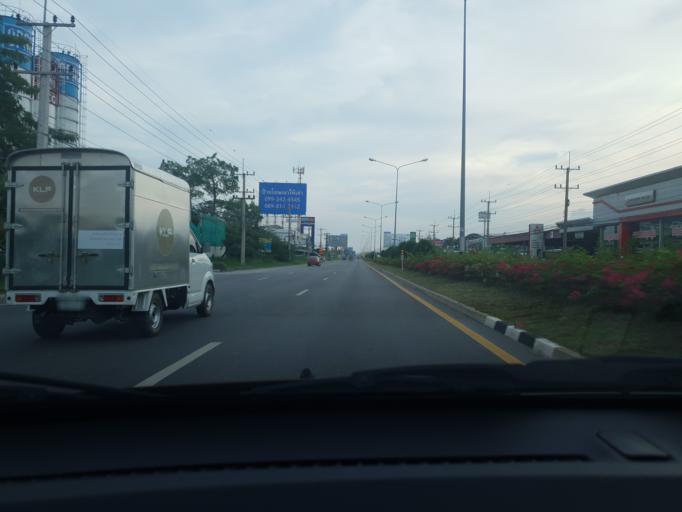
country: TH
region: Phetchaburi
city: Cha-am
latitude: 12.7790
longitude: 99.9676
